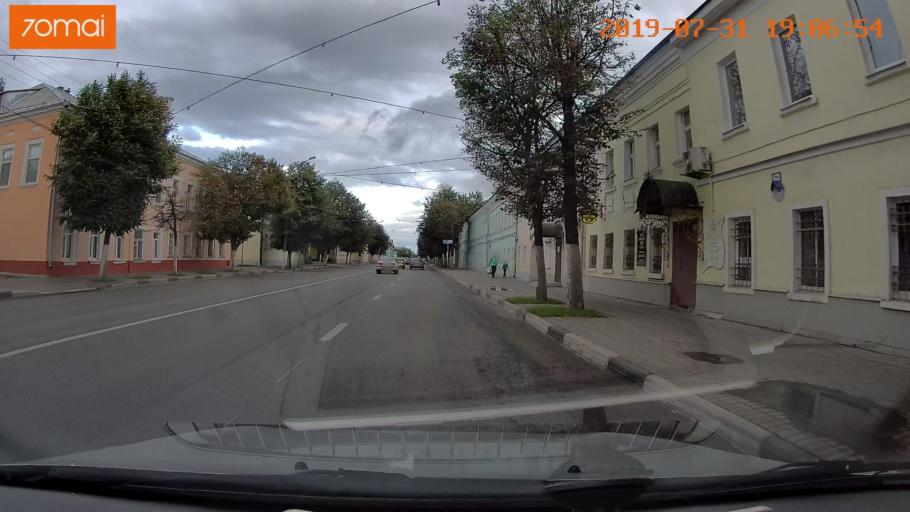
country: RU
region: Moskovskaya
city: Kolomna
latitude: 55.1000
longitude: 38.7575
